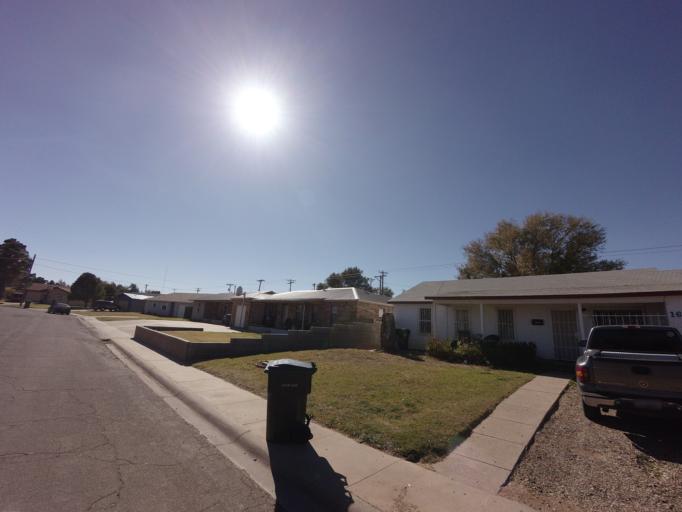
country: US
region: New Mexico
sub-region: Curry County
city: Clovis
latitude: 34.4276
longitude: -103.2049
